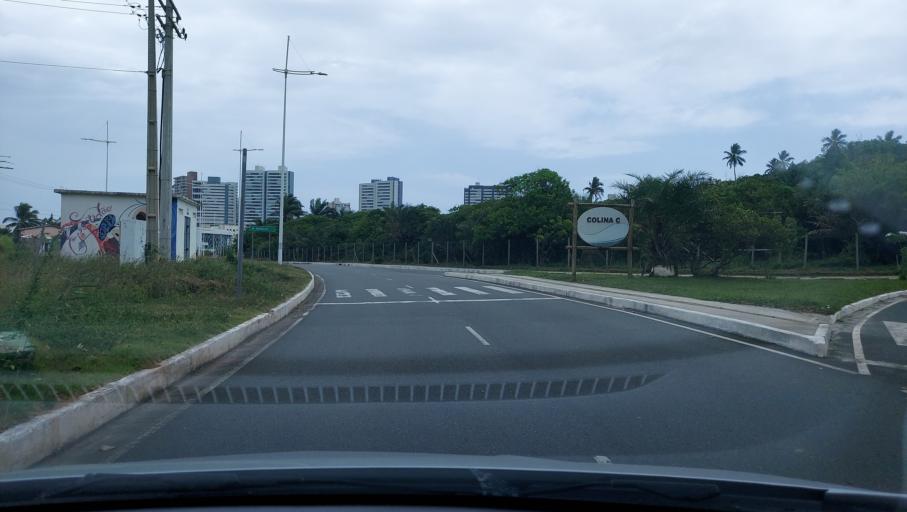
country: BR
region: Bahia
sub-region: Lauro De Freitas
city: Lauro de Freitas
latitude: -12.9553
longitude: -38.3984
